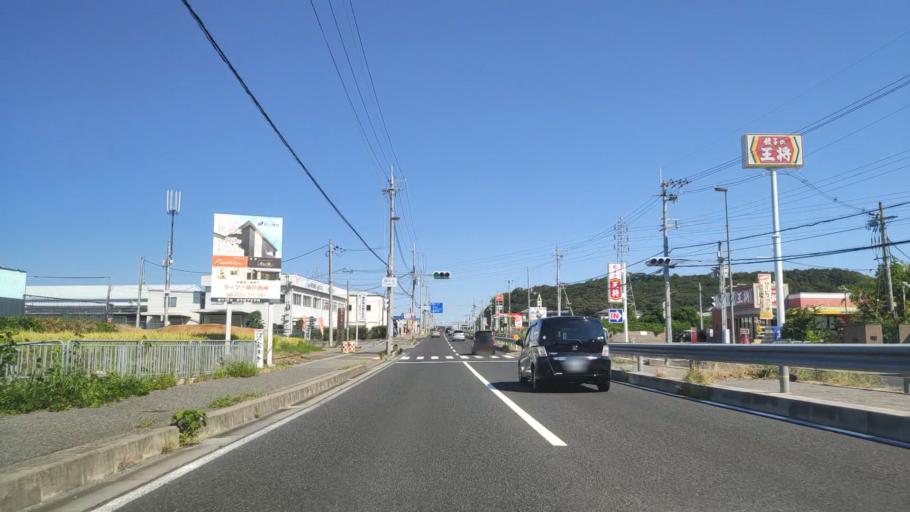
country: JP
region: Hyogo
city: Akashi
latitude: 34.7004
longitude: 134.9828
